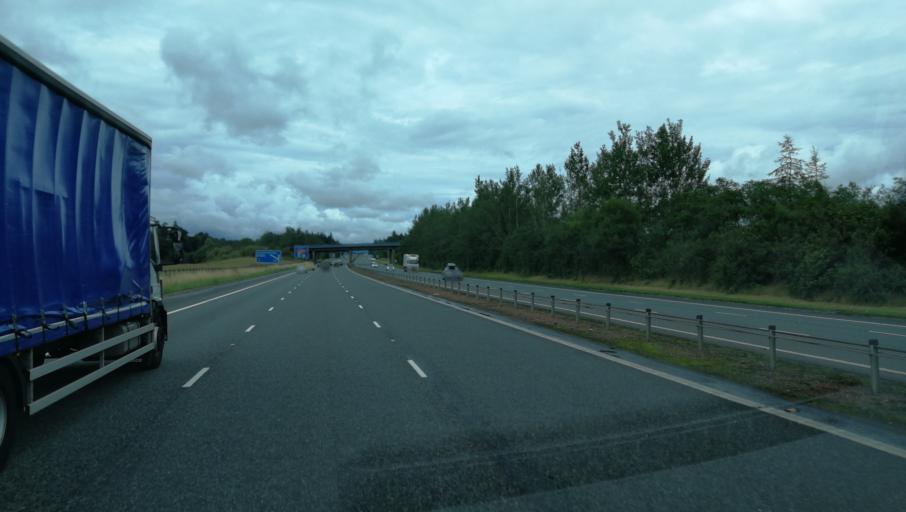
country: GB
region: Scotland
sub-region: Dumfries and Galloway
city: Lochmaben
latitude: 55.2060
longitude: -3.4125
